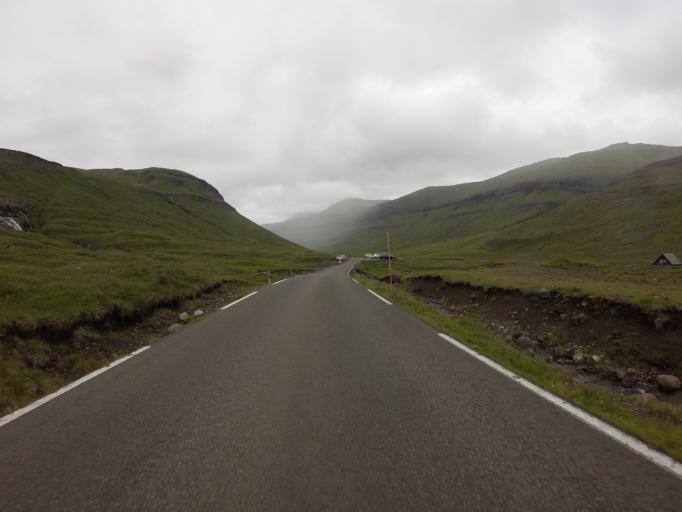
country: FO
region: Streymoy
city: Vestmanna
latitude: 62.2219
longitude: -7.1286
